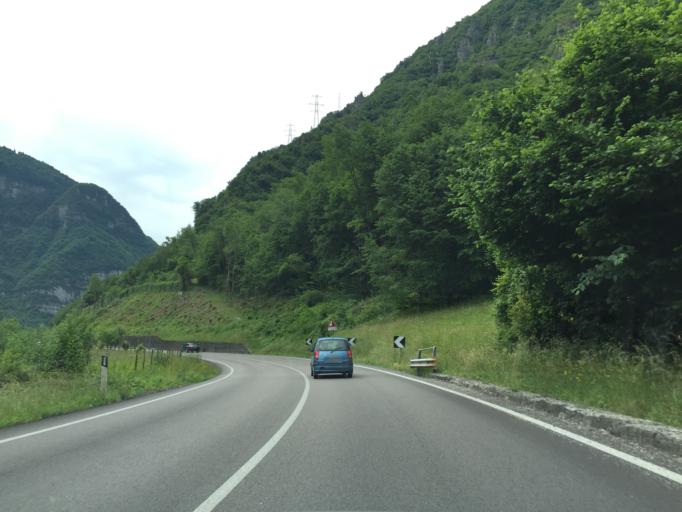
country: IT
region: Veneto
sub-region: Provincia di Belluno
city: Vas
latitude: 45.9654
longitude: 11.9319
